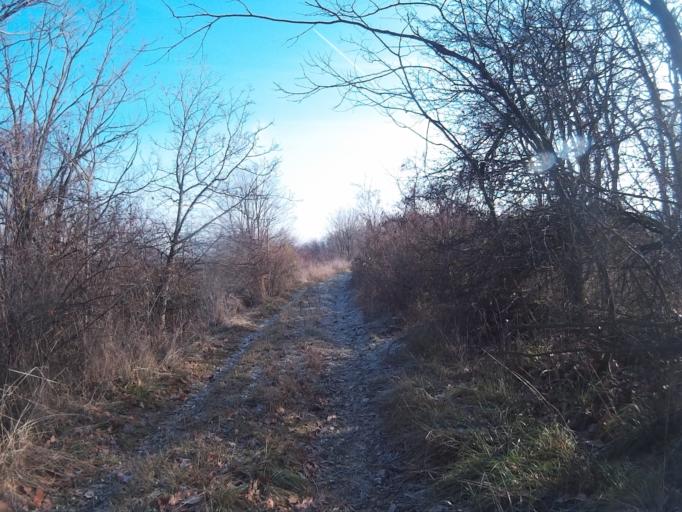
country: HU
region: Nograd
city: Bercel
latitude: 47.9311
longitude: 19.4187
